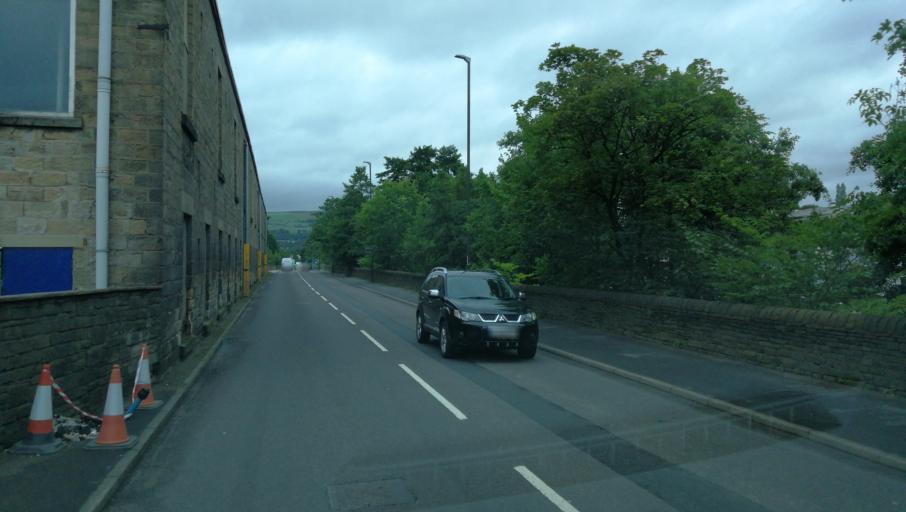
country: GB
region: England
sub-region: Borough of Tameside
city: Longdendale
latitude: 53.4499
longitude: -1.9784
